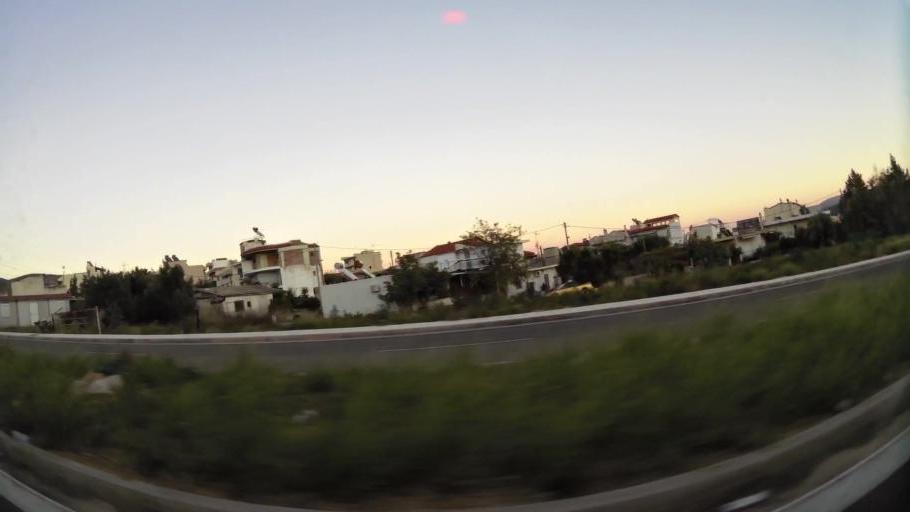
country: GR
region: Attica
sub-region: Nomarchia Dytikis Attikis
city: Ano Liosia
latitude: 38.0846
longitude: 23.6817
